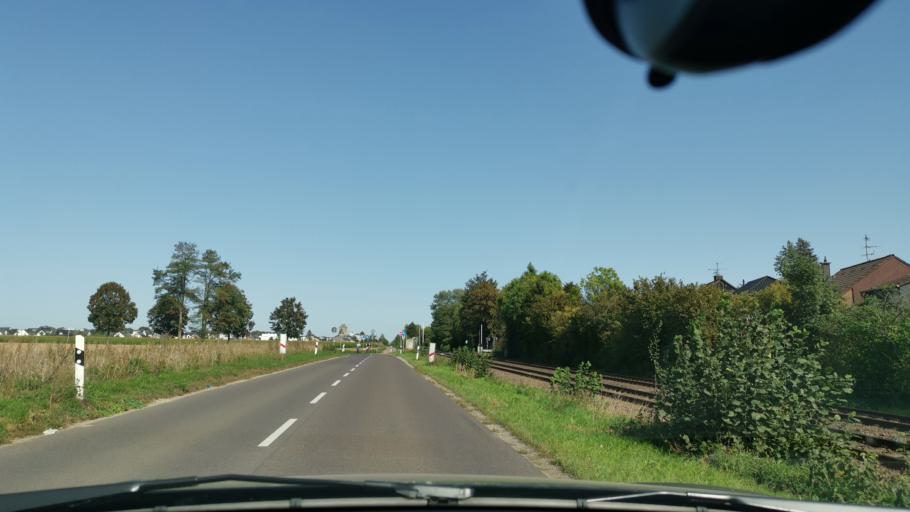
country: DE
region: North Rhine-Westphalia
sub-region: Regierungsbezirk Dusseldorf
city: Neubrueck
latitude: 51.1224
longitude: 6.6085
